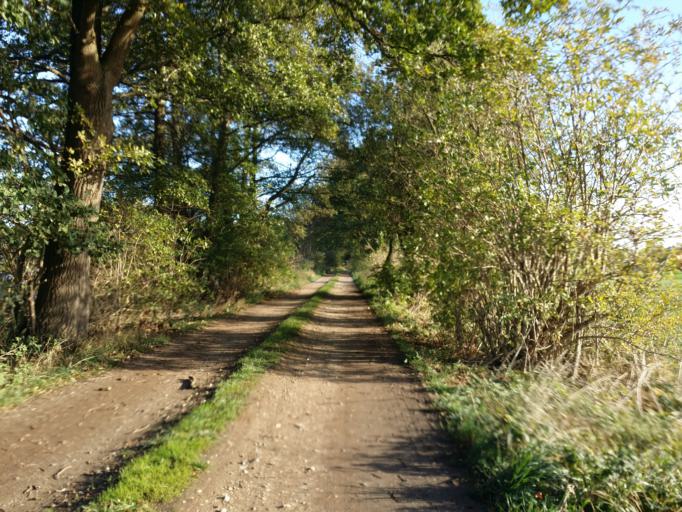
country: DE
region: Lower Saxony
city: Tarmstedt
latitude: 53.1981
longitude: 9.0538
